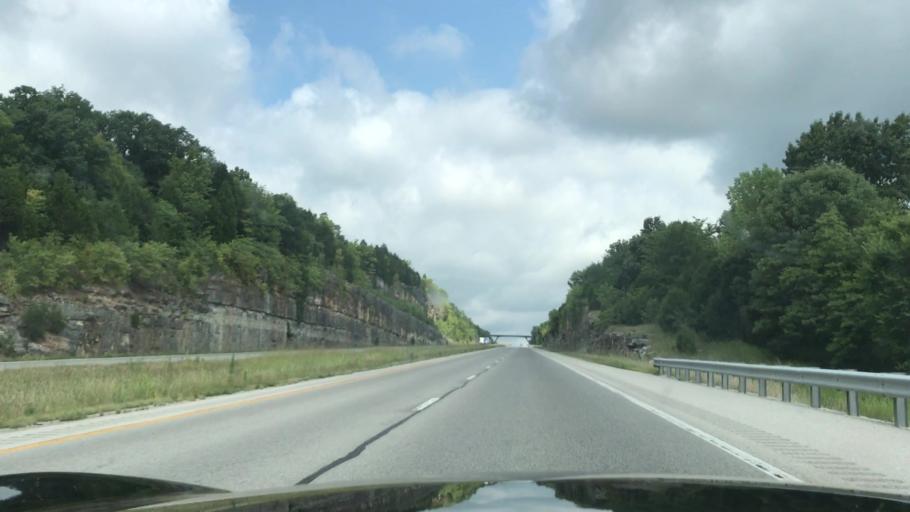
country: US
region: Kentucky
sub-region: Warren County
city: Bowling Green
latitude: 37.0127
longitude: -86.5145
